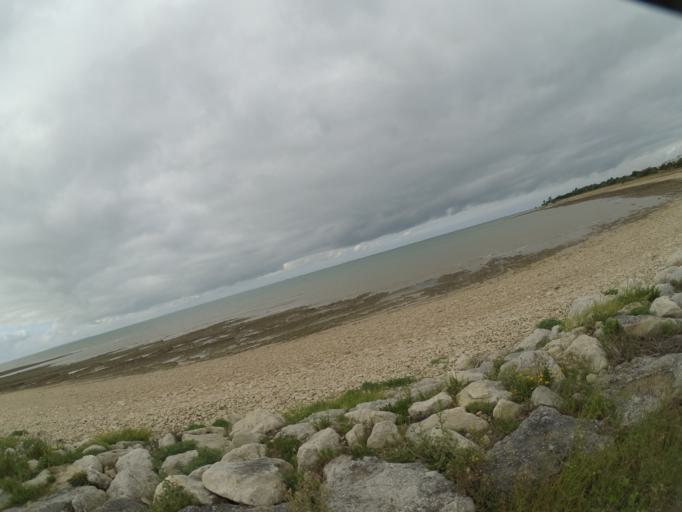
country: FR
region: Poitou-Charentes
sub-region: Departement de la Charente-Maritime
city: La Rochelle
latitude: 46.1366
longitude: -1.1528
